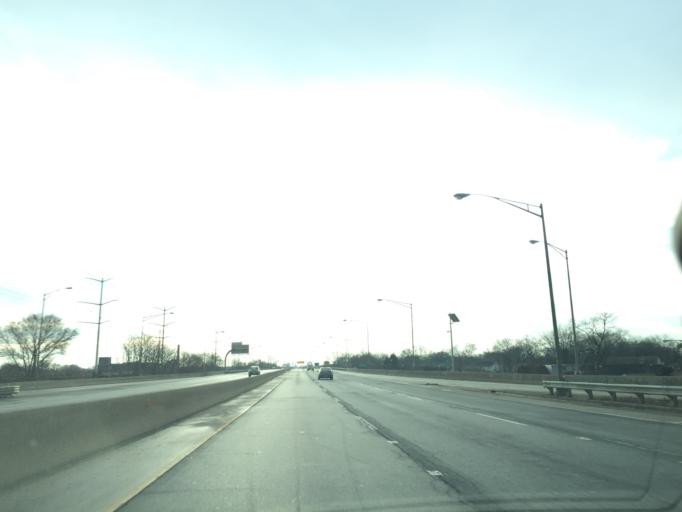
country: US
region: Illinois
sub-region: Cook County
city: Dolton
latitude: 41.7477
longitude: -87.5830
